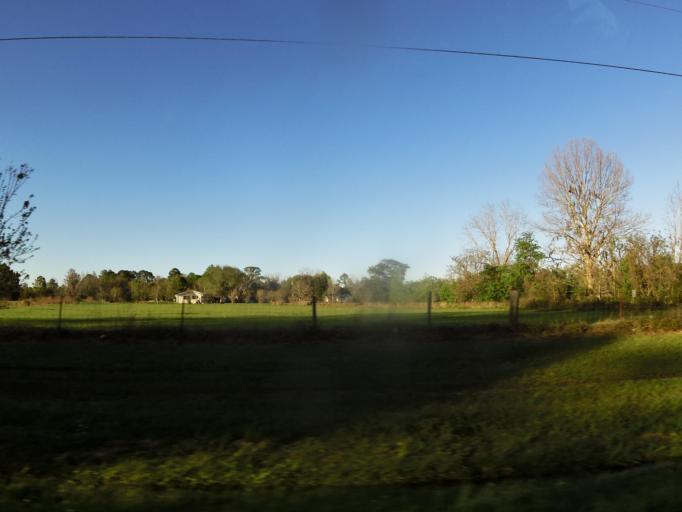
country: US
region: Florida
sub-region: Clay County
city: Keystone Heights
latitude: 29.8441
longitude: -82.0732
